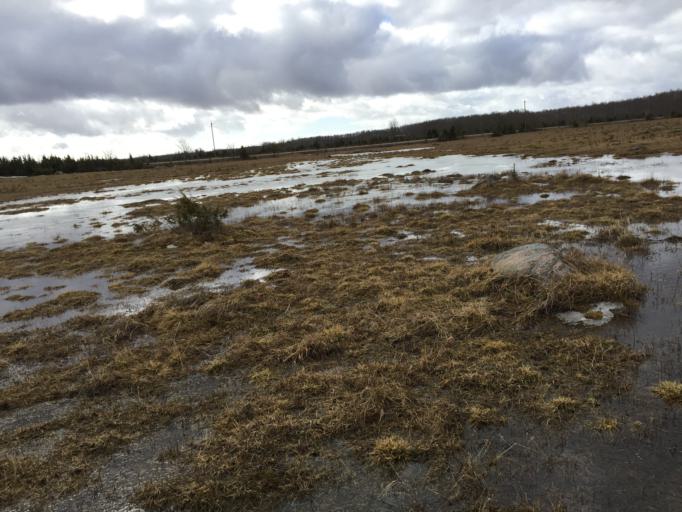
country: EE
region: Laeaene
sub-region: Ridala Parish
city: Uuemoisa
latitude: 58.7268
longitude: 23.5996
